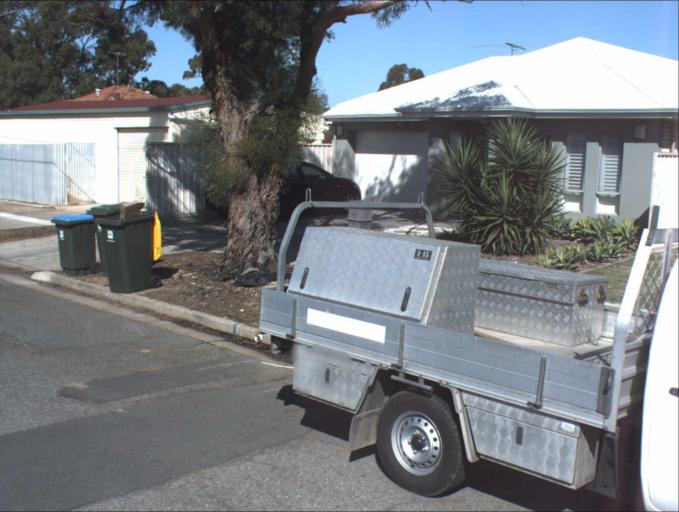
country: AU
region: South Australia
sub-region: Port Adelaide Enfield
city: Alberton
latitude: -34.8433
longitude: 138.5358
